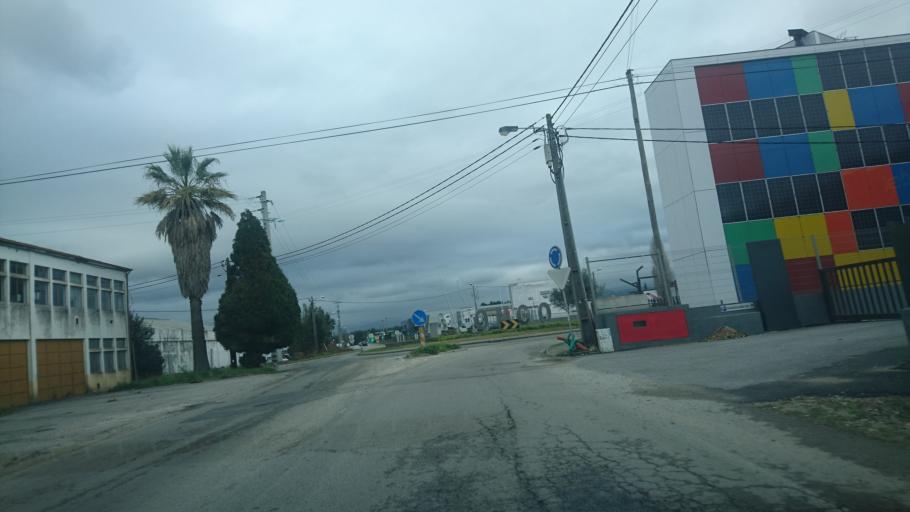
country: PT
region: Aveiro
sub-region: Agueda
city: Valongo
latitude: 40.5992
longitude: -8.4466
